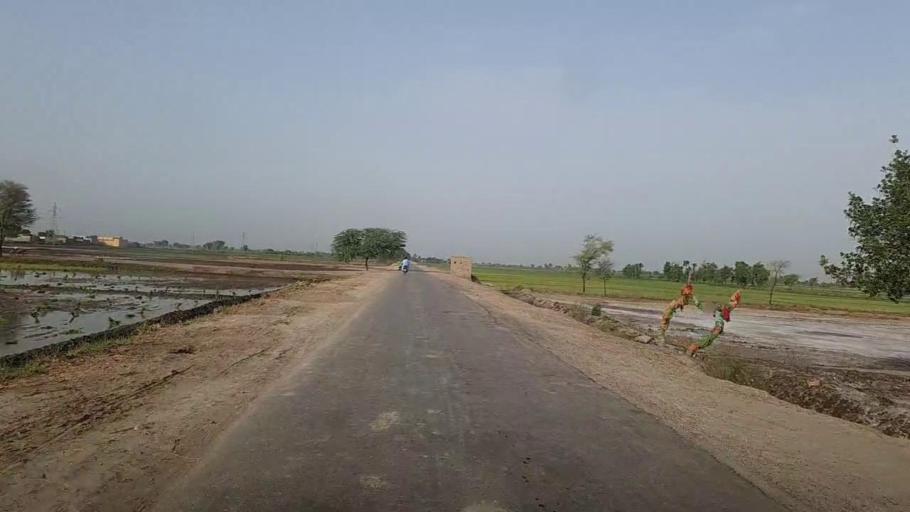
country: PK
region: Sindh
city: Mehar
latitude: 27.1565
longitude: 67.8063
